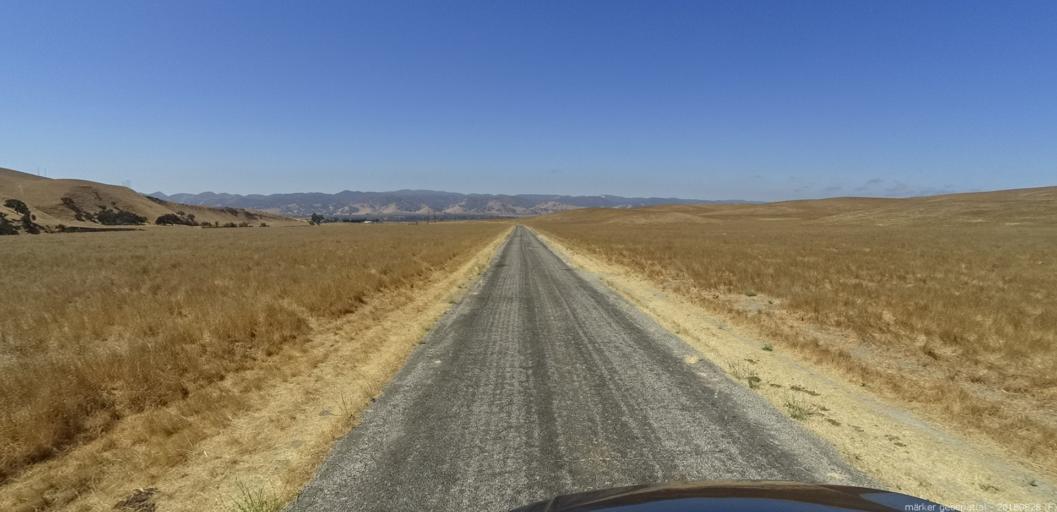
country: US
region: California
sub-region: San Luis Obispo County
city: Lake Nacimiento
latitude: 36.0269
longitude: -120.8706
